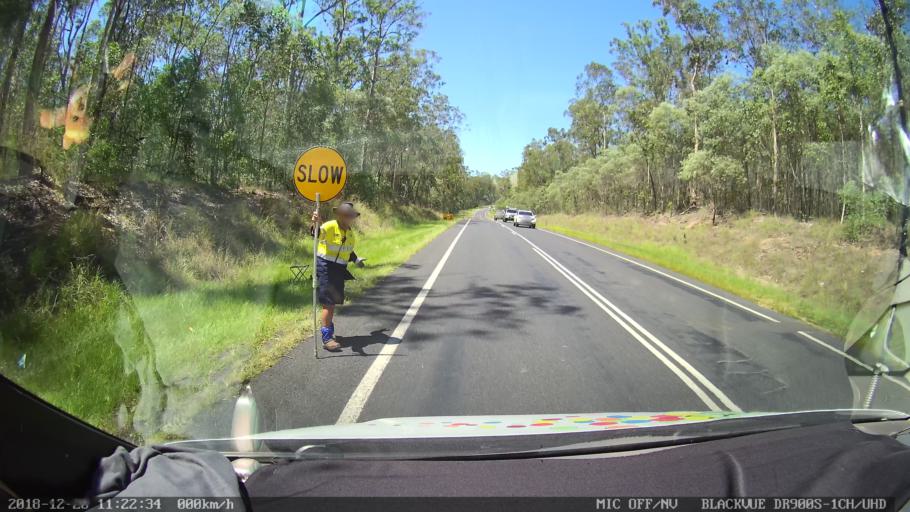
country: AU
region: New South Wales
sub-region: Richmond Valley
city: Casino
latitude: -29.0612
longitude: 153.0050
